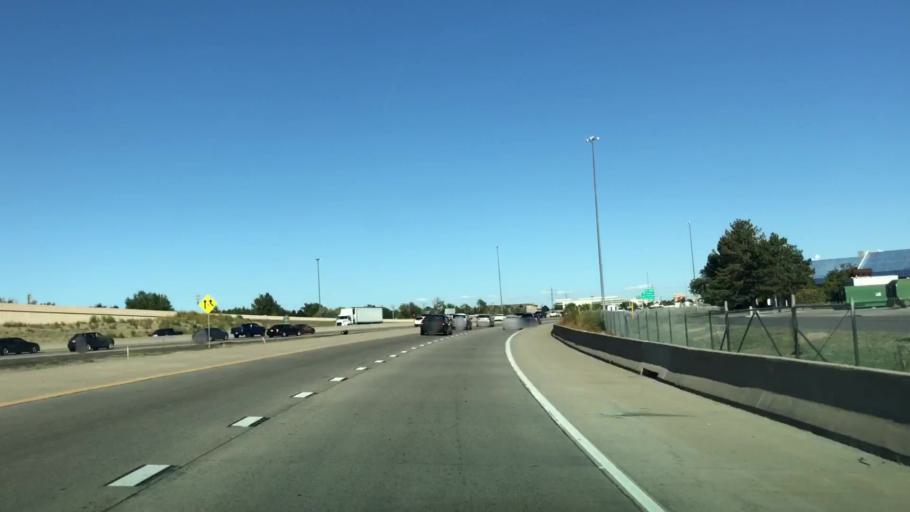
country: US
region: Colorado
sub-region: Adams County
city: Aurora
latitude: 39.7716
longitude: -104.8243
